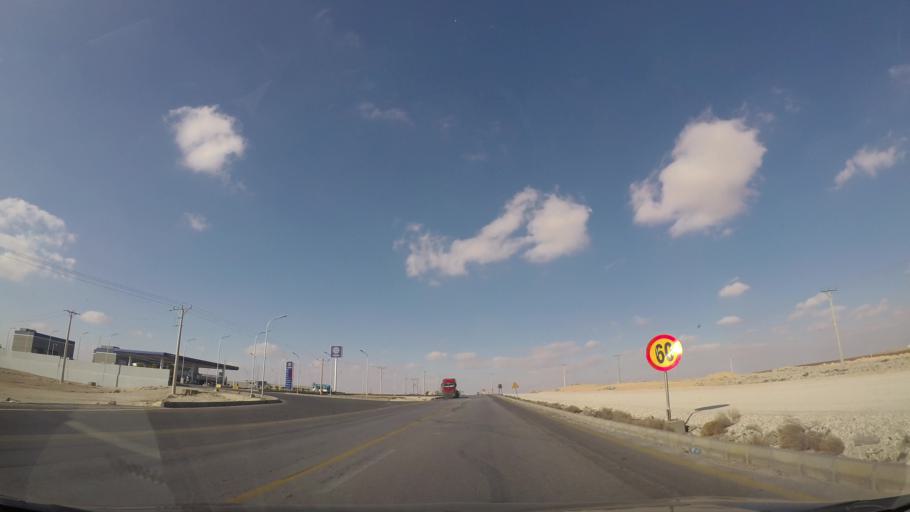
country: JO
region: Karak
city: Adir
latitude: 31.2791
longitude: 36.0544
